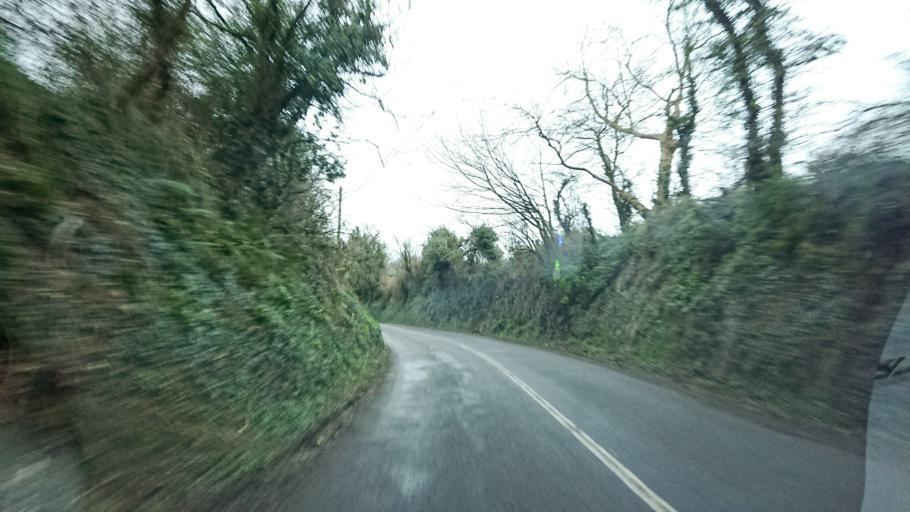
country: IE
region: Munster
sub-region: Waterford
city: Portlaw
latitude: 52.1743
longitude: -7.4041
